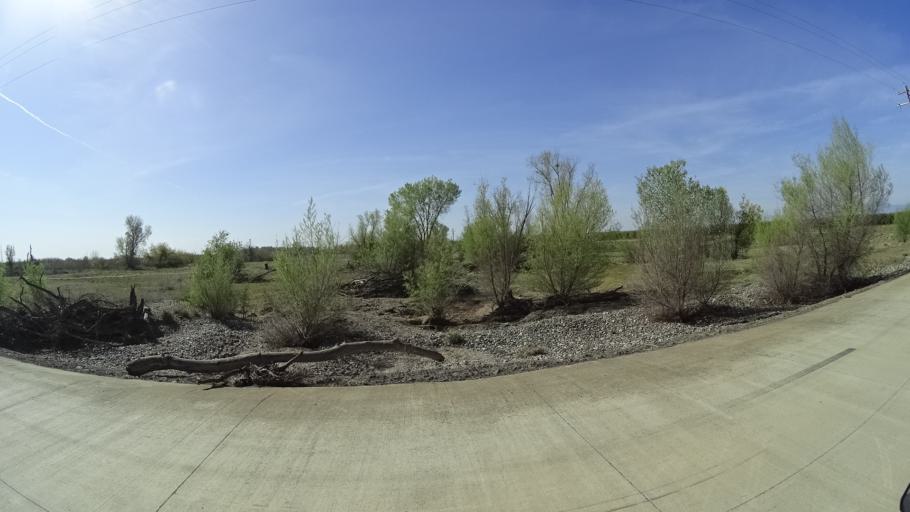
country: US
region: California
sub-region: Glenn County
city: Willows
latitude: 39.6115
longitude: -122.2019
